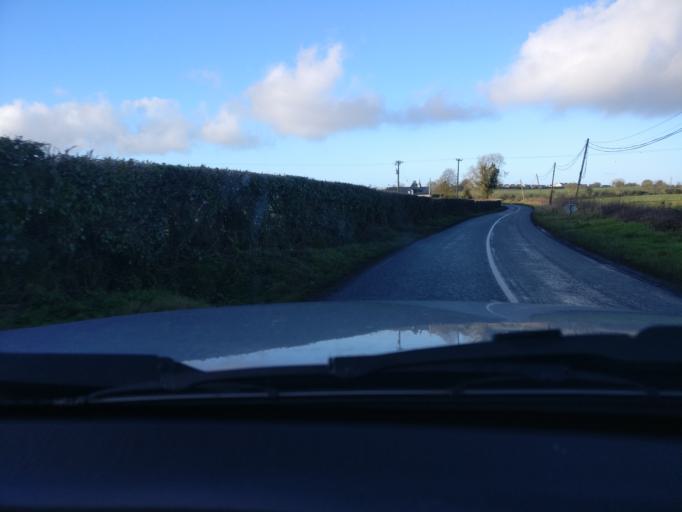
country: IE
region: Ulster
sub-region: An Cabhan
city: Mullagh
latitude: 53.7055
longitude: -7.0125
